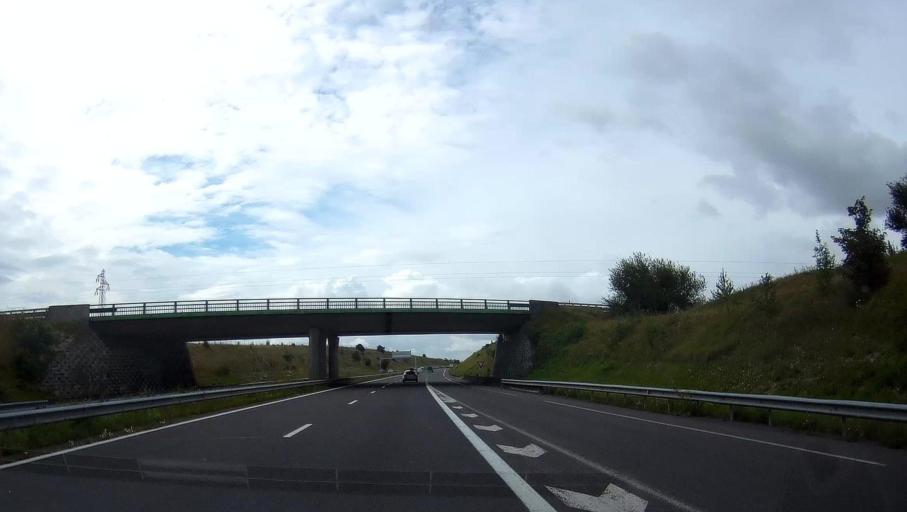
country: FR
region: Champagne-Ardenne
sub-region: Departement de la Marne
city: Fagnieres
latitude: 48.9491
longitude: 4.2893
